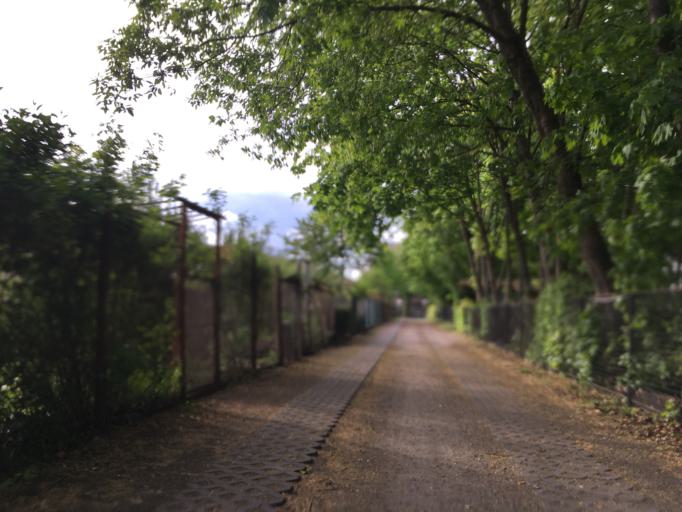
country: DE
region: Berlin
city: Heinersdorf
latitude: 52.5578
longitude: 13.4470
